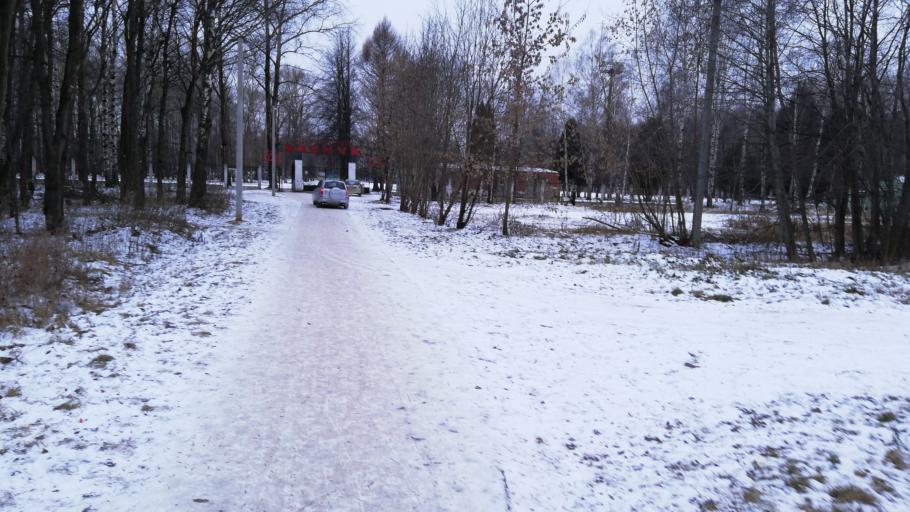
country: RU
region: Jaroslavl
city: Yaroslavl
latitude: 57.7248
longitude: 39.8176
